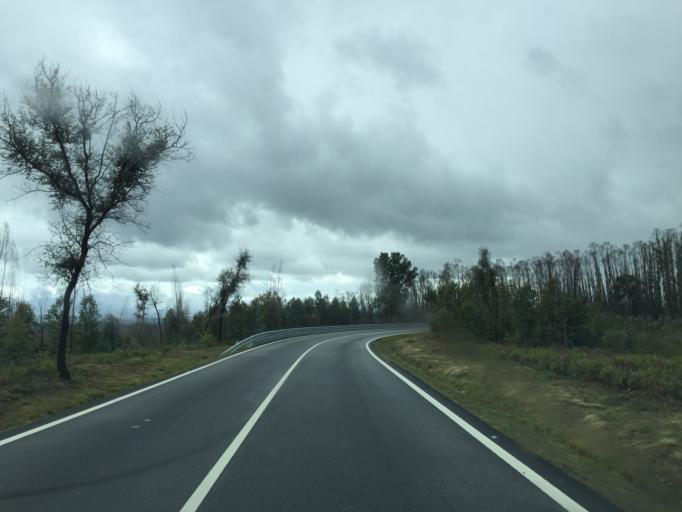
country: PT
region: Coimbra
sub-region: Tabua
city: Tabua
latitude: 40.3280
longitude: -7.9515
